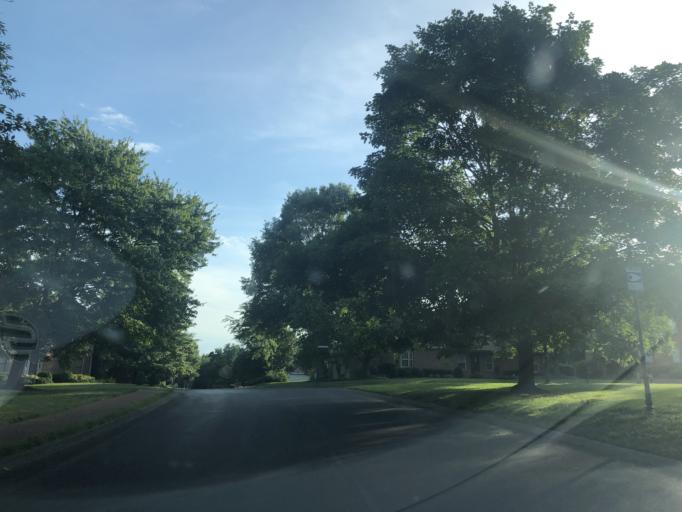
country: US
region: Tennessee
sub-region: Davidson County
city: Belle Meade
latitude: 36.0598
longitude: -86.9220
